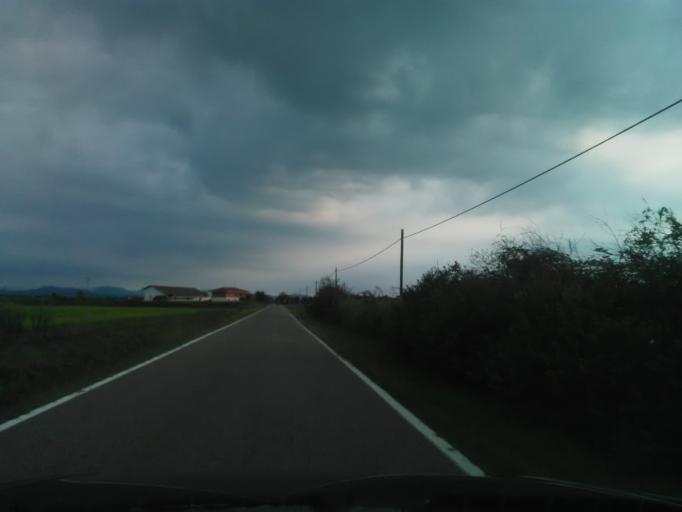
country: IT
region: Piedmont
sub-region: Provincia di Vercelli
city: Rovasenda
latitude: 45.5202
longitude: 8.2995
